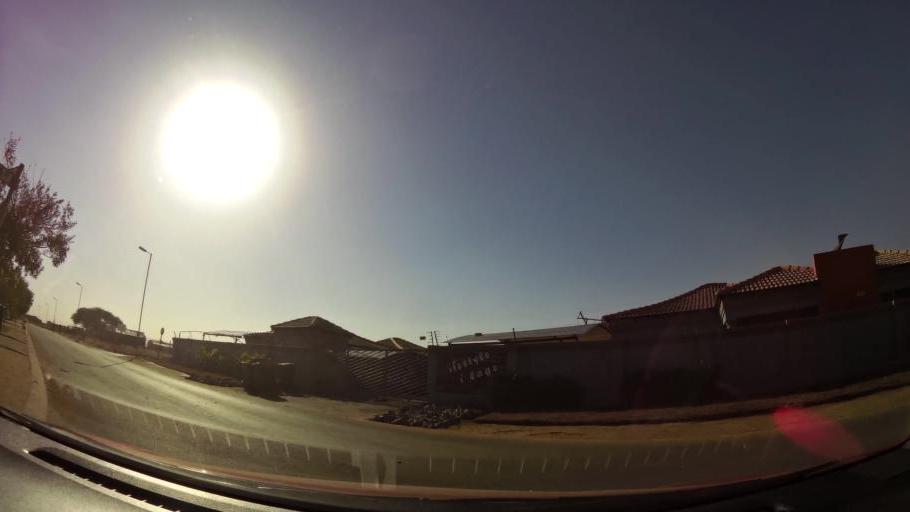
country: ZA
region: Gauteng
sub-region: City of Tshwane Metropolitan Municipality
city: Mabopane
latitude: -25.5767
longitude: 28.0960
